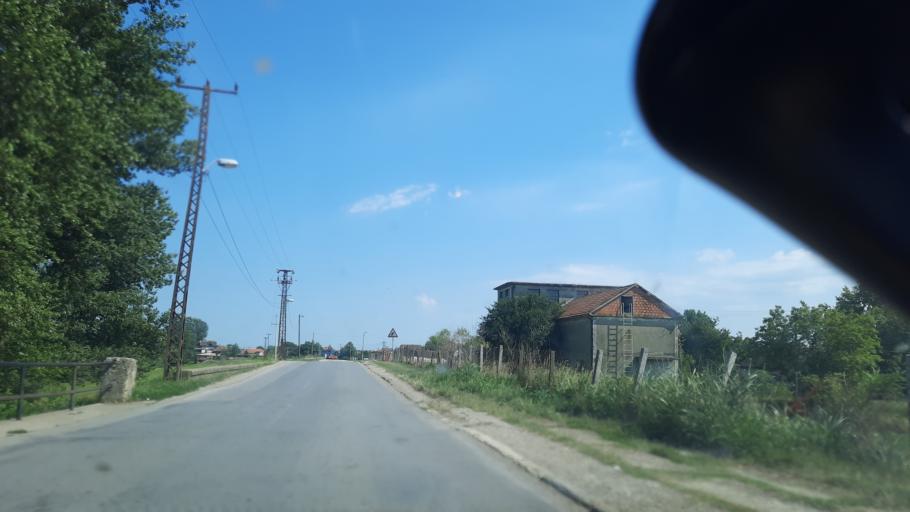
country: RS
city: Macvanska Mitrovica
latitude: 44.9607
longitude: 19.6035
